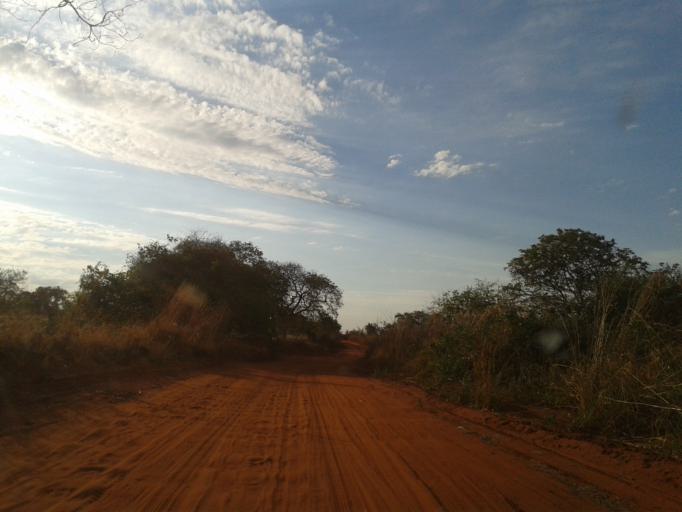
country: BR
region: Minas Gerais
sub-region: Ituiutaba
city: Ituiutaba
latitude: -19.0214
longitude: -49.3528
